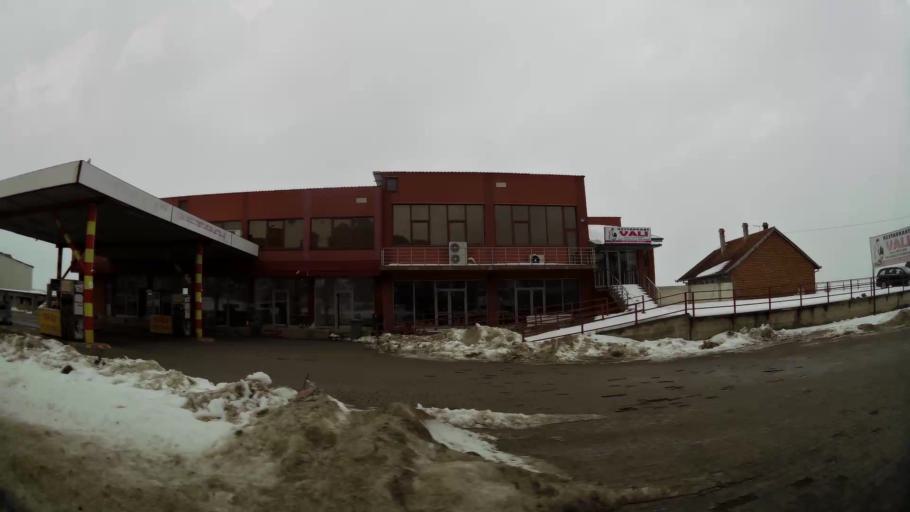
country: XK
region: Pristina
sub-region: Komuna e Prishtines
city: Pristina
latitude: 42.7279
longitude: 21.1440
